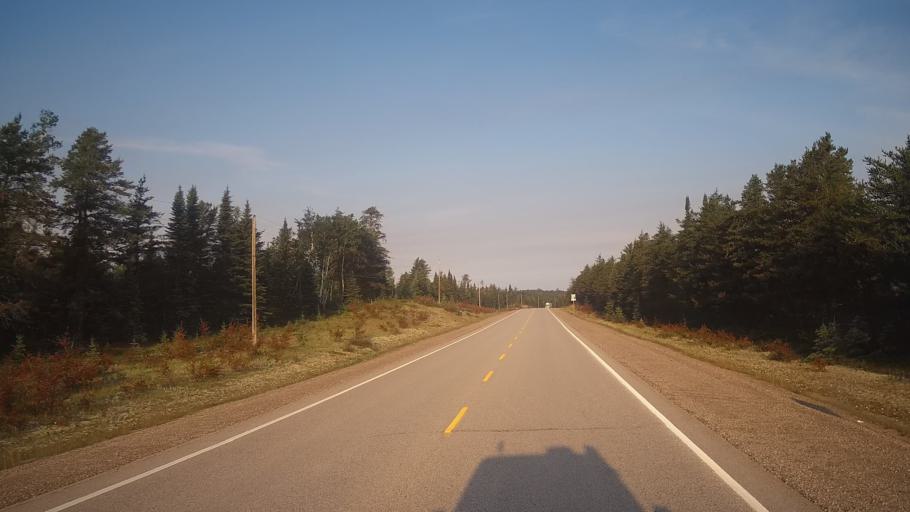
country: CA
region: Ontario
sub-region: Rainy River District
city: Atikokan
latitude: 49.2607
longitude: -91.1694
